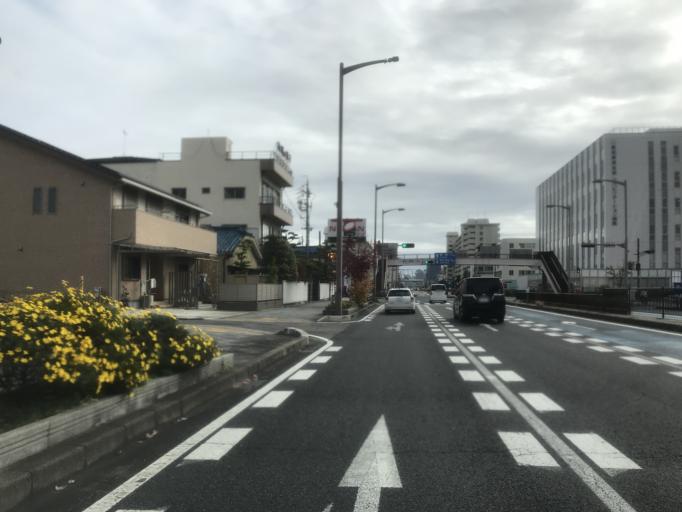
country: JP
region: Aichi
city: Nagoya-shi
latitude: 35.1873
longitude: 136.8778
